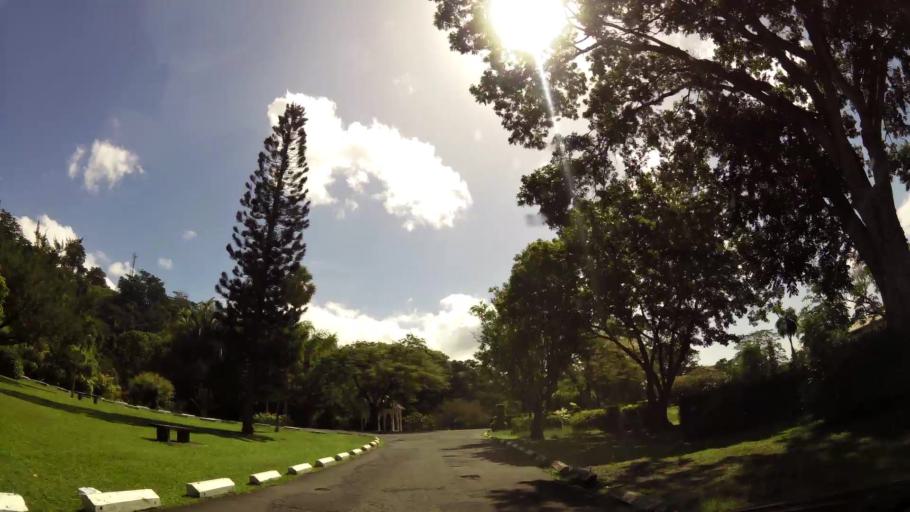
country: DM
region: Saint George
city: Roseau
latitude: 15.3000
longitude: -61.3828
